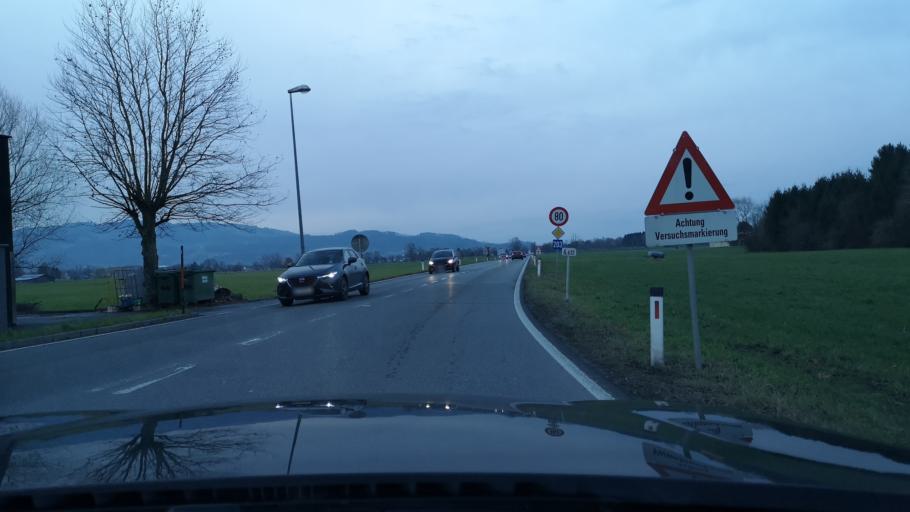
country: CH
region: Saint Gallen
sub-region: Wahlkreis Rheintal
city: Diepoldsau
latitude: 47.3982
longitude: 9.6771
